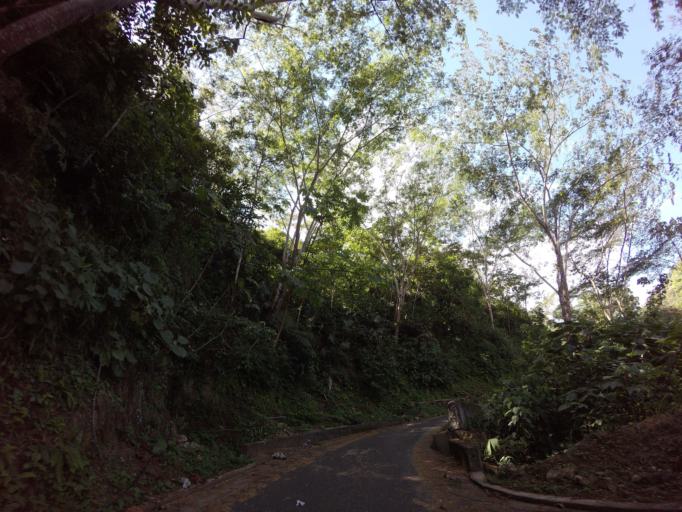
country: CO
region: Caldas
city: Norcasia
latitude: 5.5707
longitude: -74.9020
